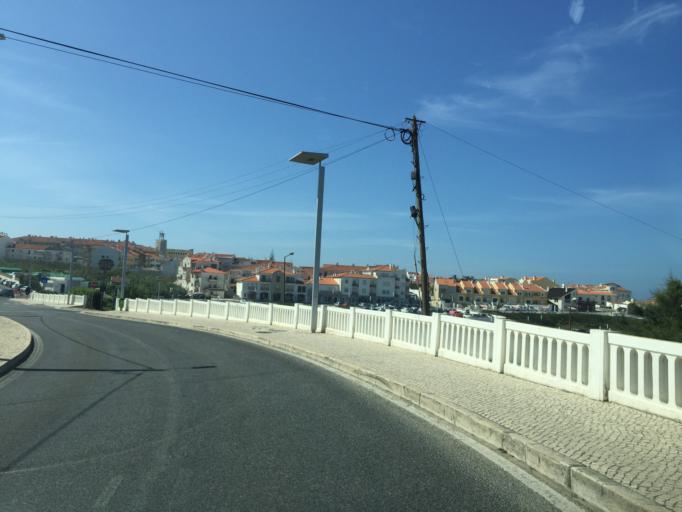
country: PT
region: Lisbon
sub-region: Torres Vedras
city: Silveira
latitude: 39.1378
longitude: -9.3793
